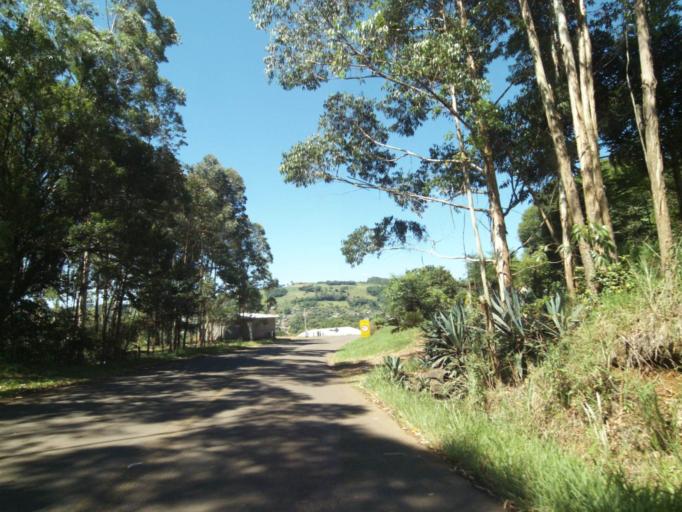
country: BR
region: Parana
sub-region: Ampere
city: Ampere
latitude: -26.1806
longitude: -53.3641
